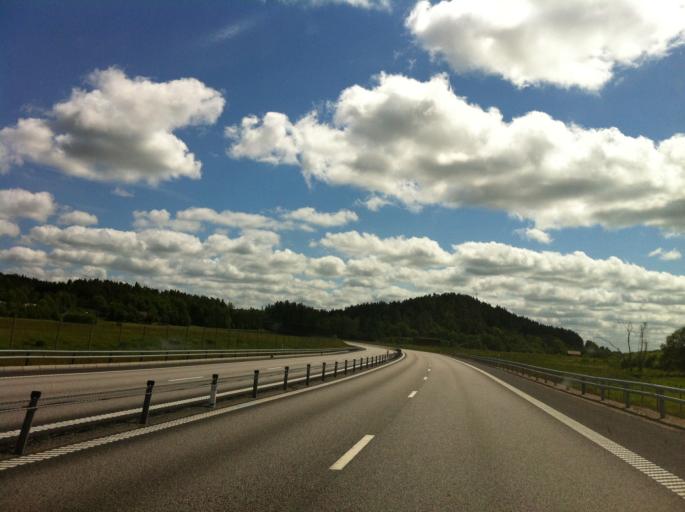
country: SE
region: Vaestra Goetaland
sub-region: Lilla Edets Kommun
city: Lodose
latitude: 58.0760
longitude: 12.1544
